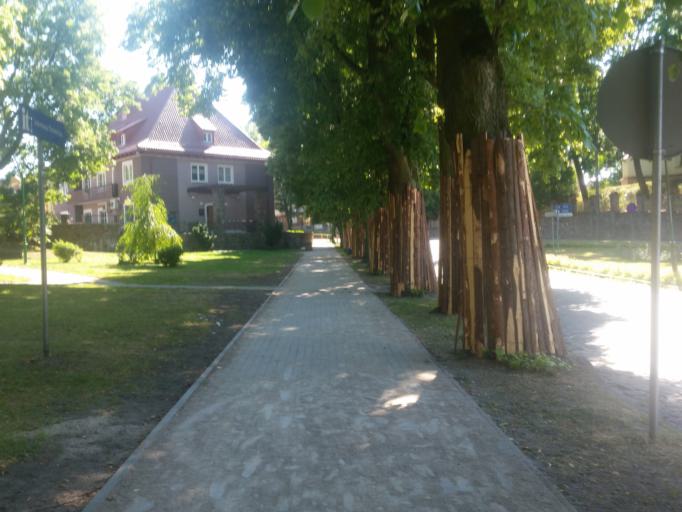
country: PL
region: Warmian-Masurian Voivodeship
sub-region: Powiat goldapski
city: Goldap
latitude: 54.3097
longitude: 22.3050
